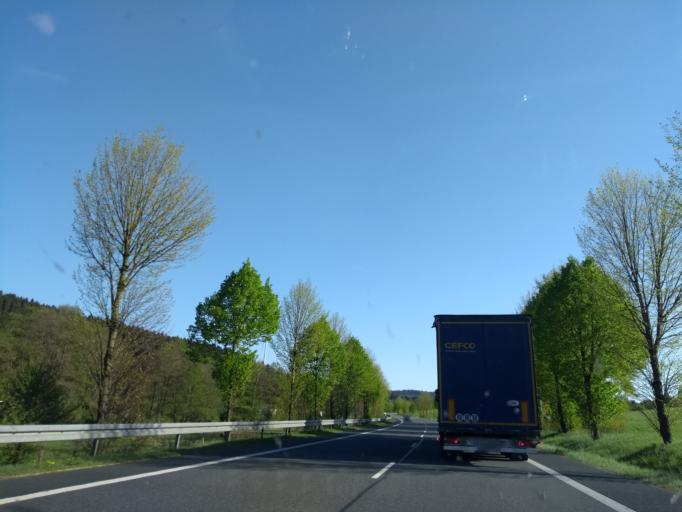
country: DE
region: Hesse
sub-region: Regierungsbezirk Giessen
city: Breidenbach
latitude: 50.8352
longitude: 8.3868
